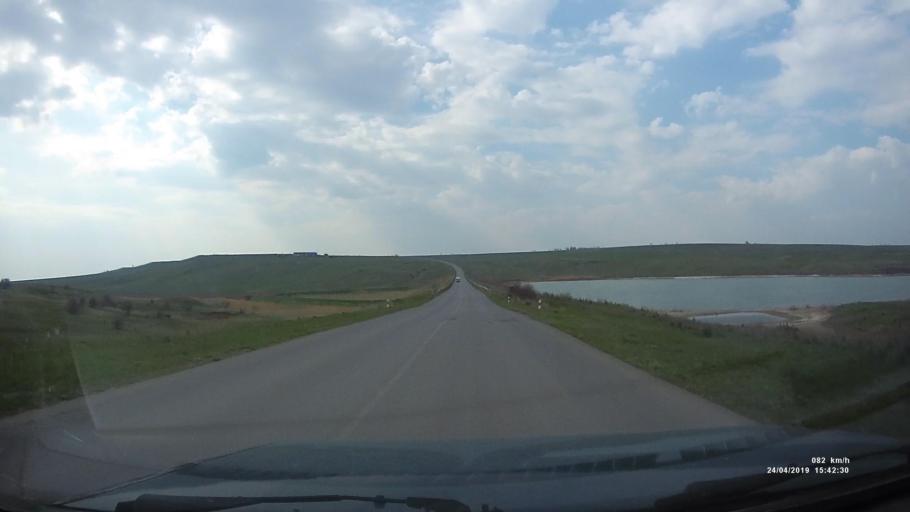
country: RU
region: Kalmykiya
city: Yashalta
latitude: 46.5766
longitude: 42.7871
